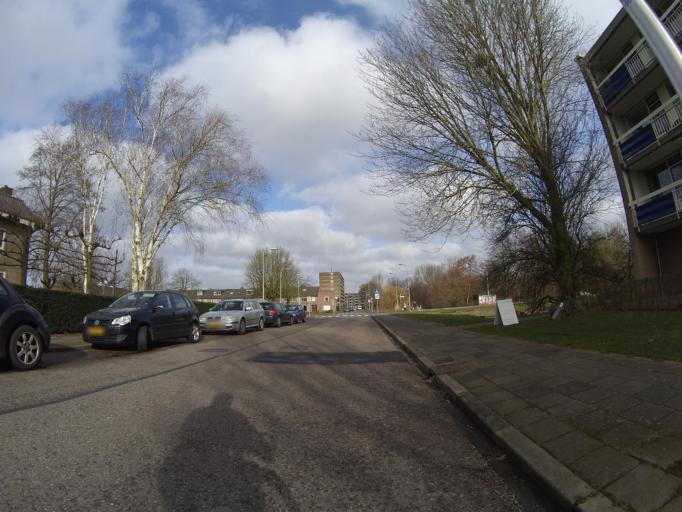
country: NL
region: Utrecht
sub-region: Gemeente Amersfoort
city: Randenbroek
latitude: 52.1654
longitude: 5.4114
